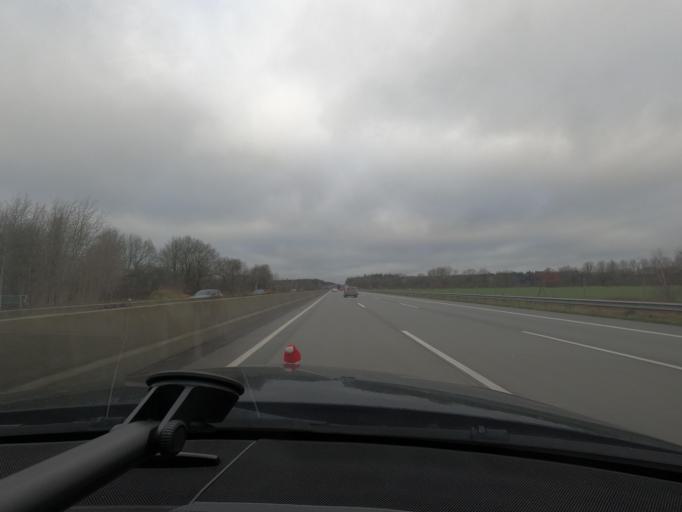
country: DE
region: Schleswig-Holstein
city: Schmalfeld
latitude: 53.8883
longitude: 9.9432
